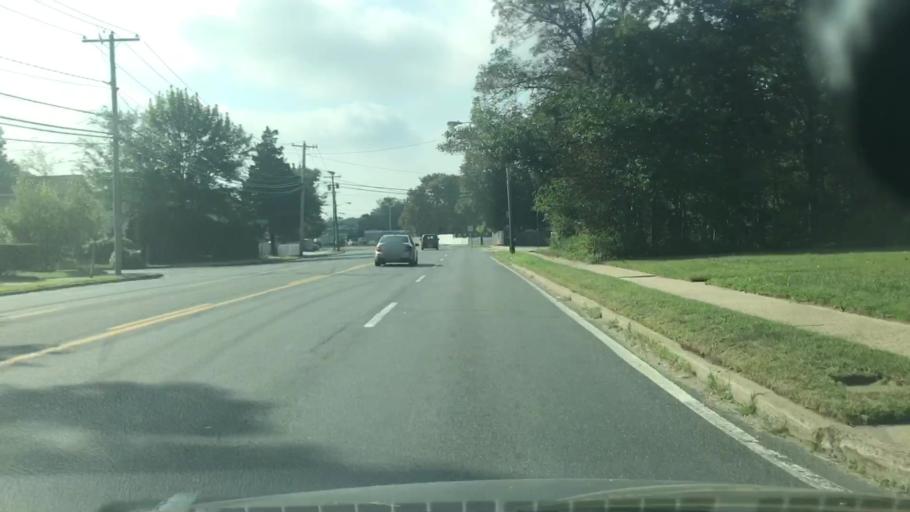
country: US
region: New York
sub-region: Suffolk County
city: North Lindenhurst
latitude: 40.7101
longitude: -73.3907
